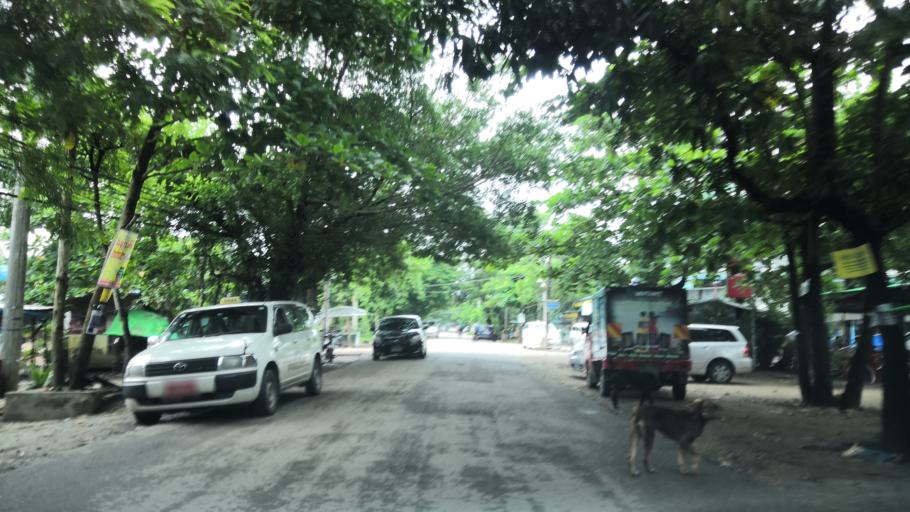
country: MM
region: Yangon
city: Yangon
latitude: 16.8871
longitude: 96.1761
